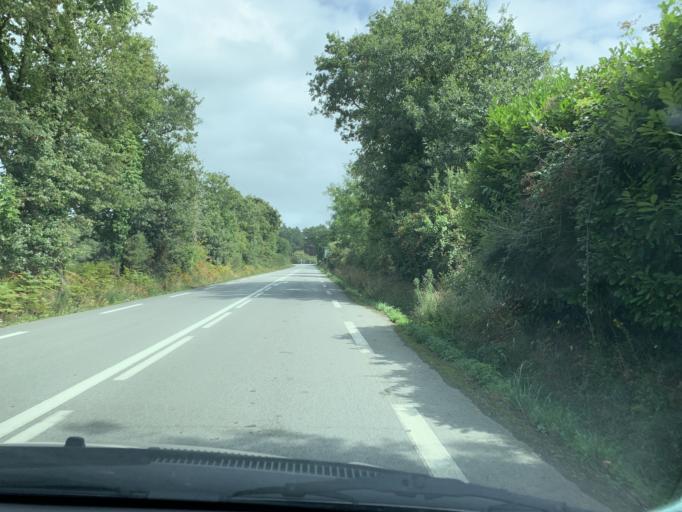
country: FR
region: Brittany
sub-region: Departement du Morbihan
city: Penestin
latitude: 47.4792
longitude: -2.4540
